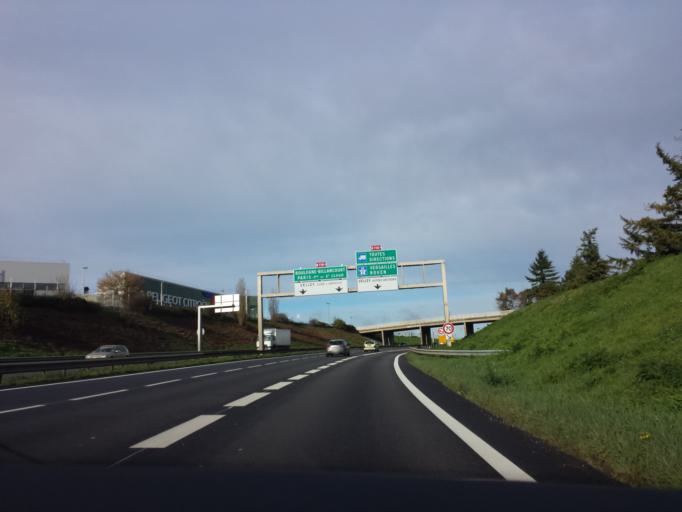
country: FR
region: Ile-de-France
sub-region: Departement de l'Essonne
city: Bievres
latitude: 48.7732
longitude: 2.2250
